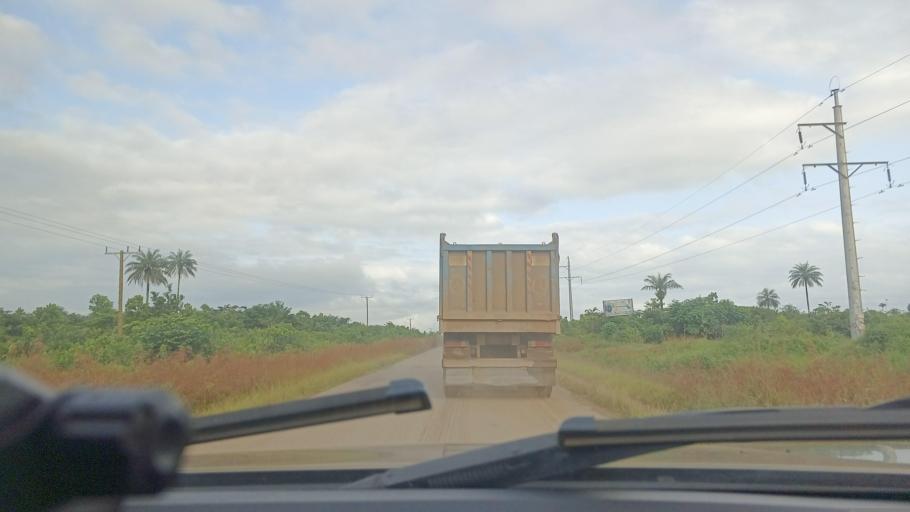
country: LR
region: Montserrado
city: Monrovia
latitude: 6.5758
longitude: -10.8844
